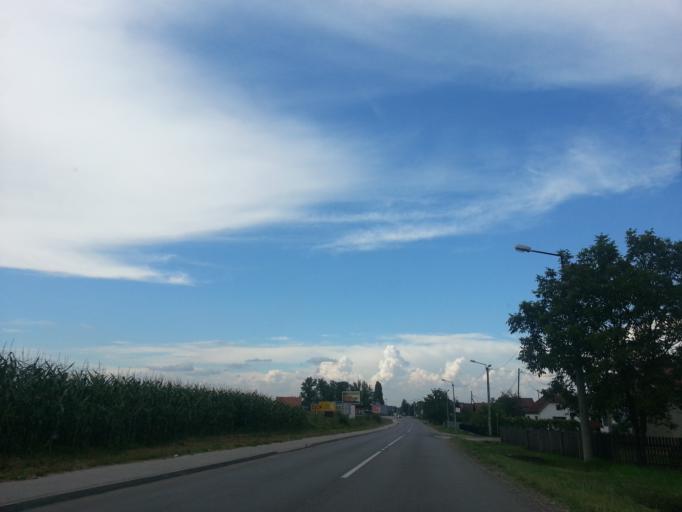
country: BA
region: Brcko
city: Brcko
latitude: 44.8388
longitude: 18.8202
